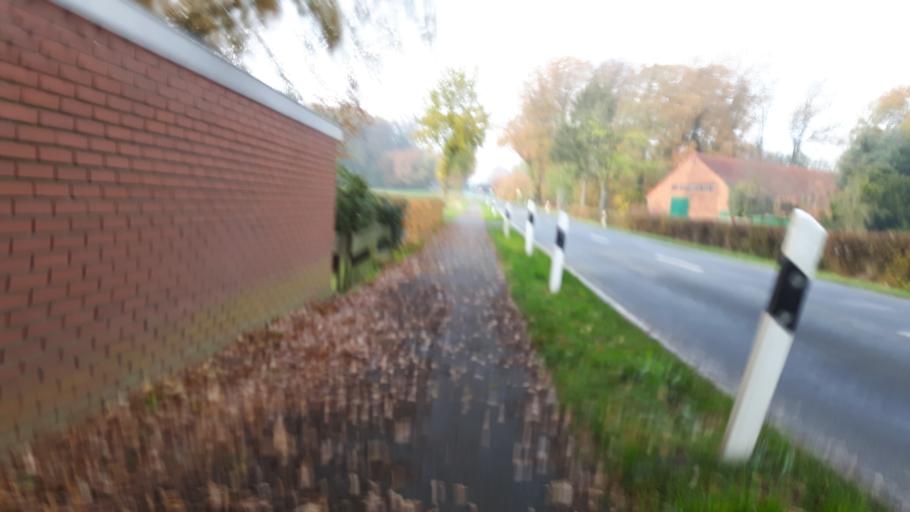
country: DE
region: Lower Saxony
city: Ganderkesee
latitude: 53.0164
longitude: 8.5794
